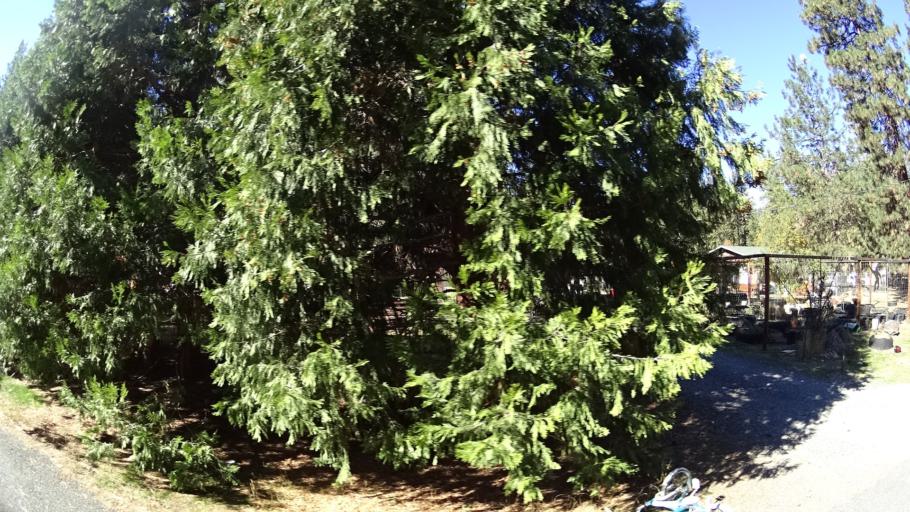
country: US
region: California
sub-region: Siskiyou County
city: Yreka
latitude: 41.5197
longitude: -122.9209
